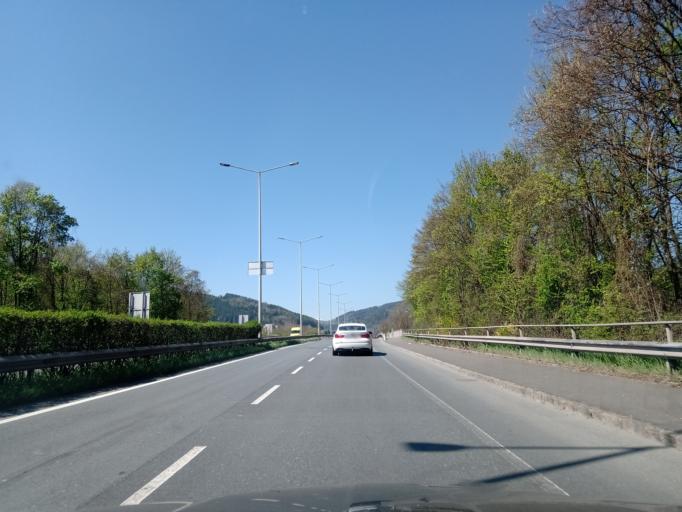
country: AT
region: Styria
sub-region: Politischer Bezirk Leoben
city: Leoben
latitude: 47.3762
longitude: 15.0860
